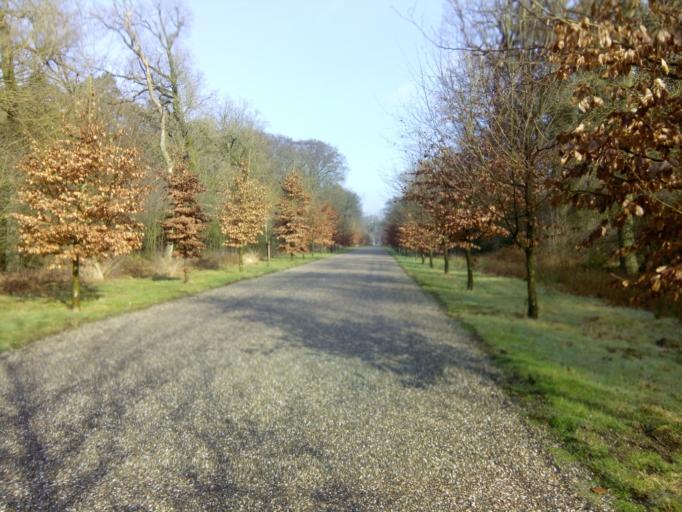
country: NL
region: Utrecht
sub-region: Gemeente Utrechtse Heuvelrug
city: Maarsbergen
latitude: 52.0445
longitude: 5.3983
